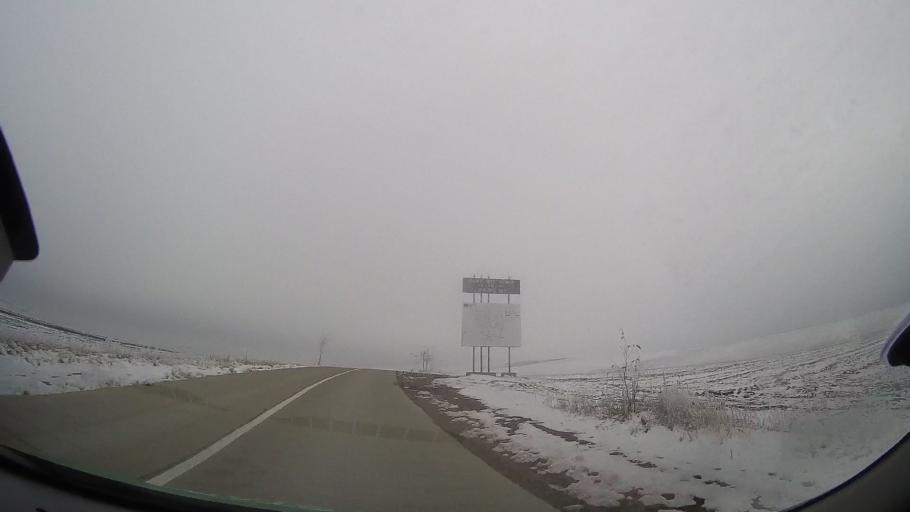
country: RO
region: Vaslui
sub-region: Comuna Ivesti
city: Ivesti
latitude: 46.2044
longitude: 27.5076
